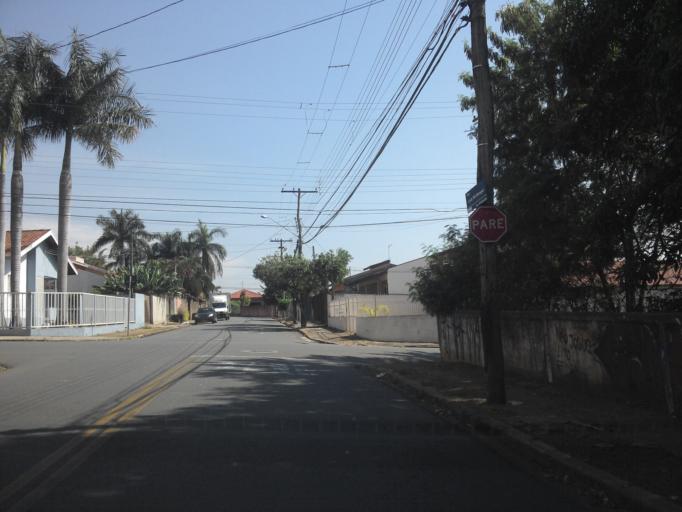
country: BR
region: Sao Paulo
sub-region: Hortolandia
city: Hortolandia
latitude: -22.8738
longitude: -47.2262
